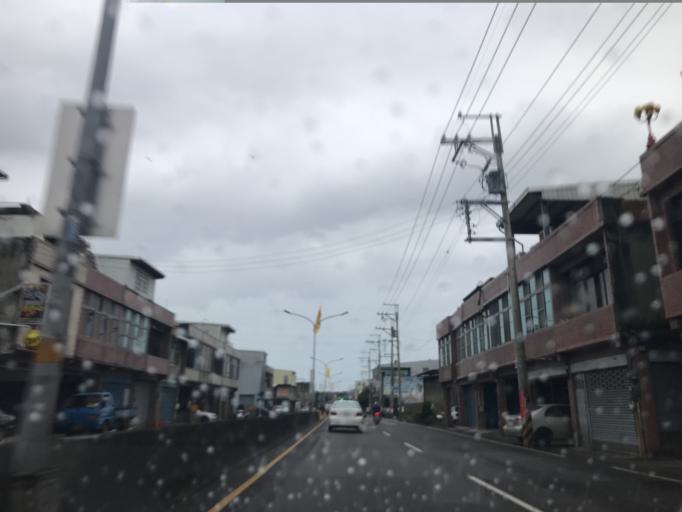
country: TW
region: Taiwan
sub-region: Hsinchu
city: Zhubei
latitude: 24.8265
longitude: 121.0526
